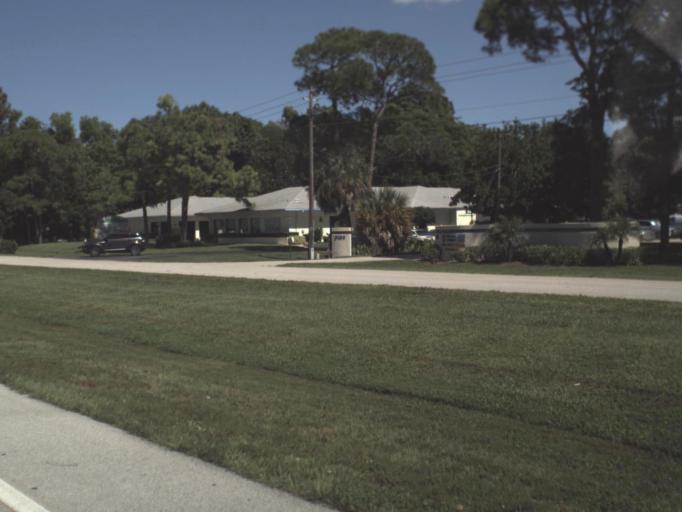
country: US
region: Florida
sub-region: Collier County
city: Pine Ridge
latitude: 26.2136
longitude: -81.8003
